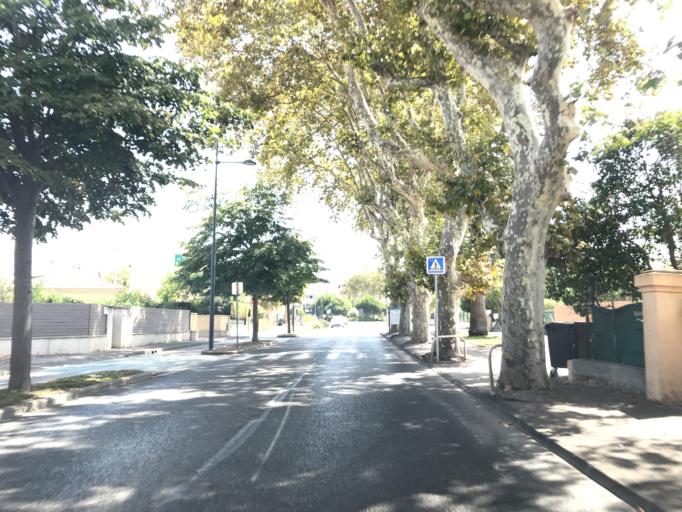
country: FR
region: Provence-Alpes-Cote d'Azur
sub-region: Departement du Var
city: Six-Fours-les-Plages
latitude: 43.0956
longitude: 5.8322
